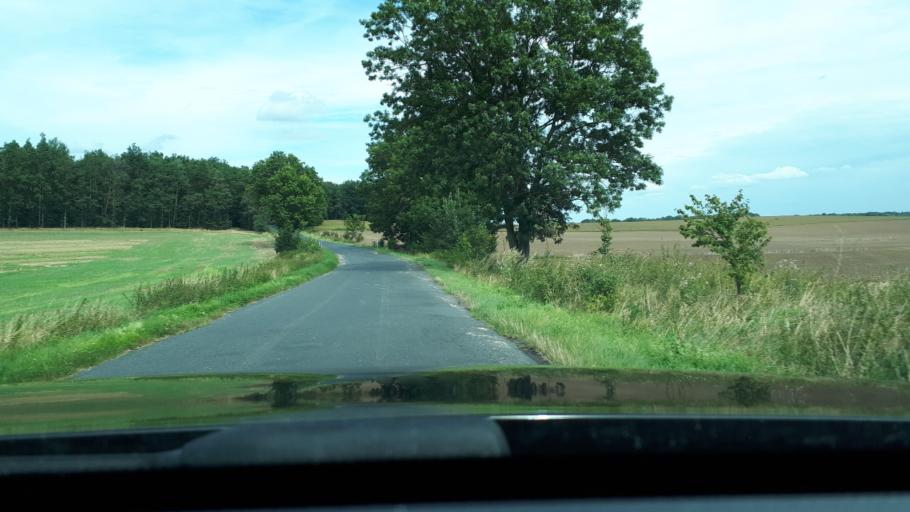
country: PL
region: Lower Silesian Voivodeship
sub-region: Powiat zlotoryjski
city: Olszanica
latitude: 51.1803
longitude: 15.7705
